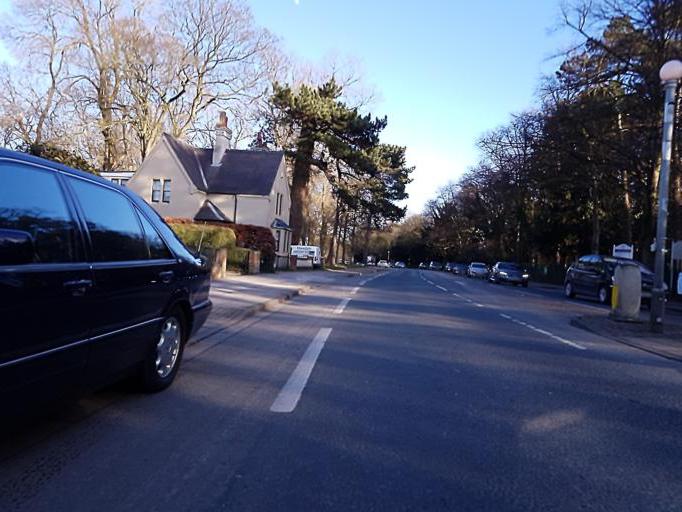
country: GB
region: England
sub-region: North East Lincolnshire
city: Grimsby
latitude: 53.5536
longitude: -0.0702
